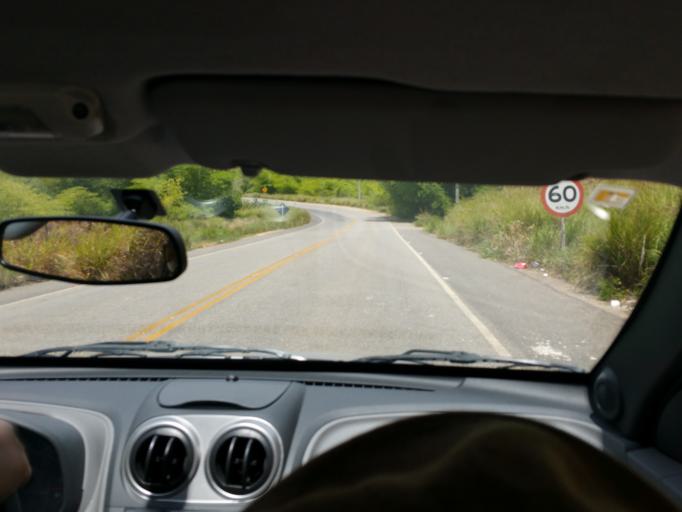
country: BR
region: Pernambuco
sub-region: Rio Formoso
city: Rio Formoso
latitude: -8.6945
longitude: -35.1296
